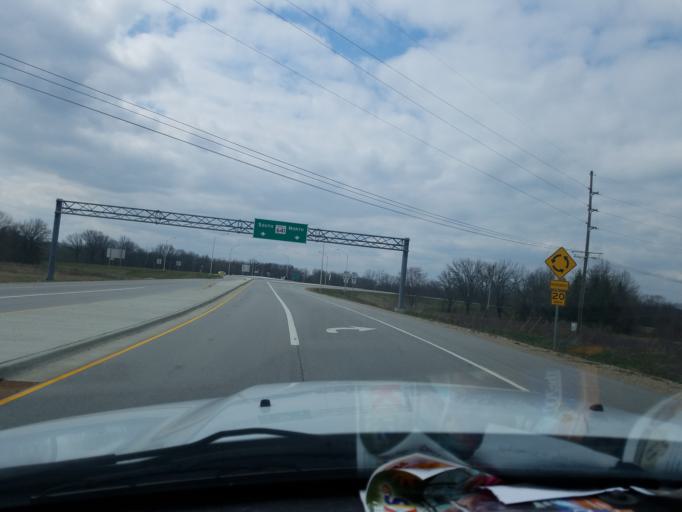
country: US
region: Indiana
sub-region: Vigo County
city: Terre Haute
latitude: 39.4114
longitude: -87.3329
